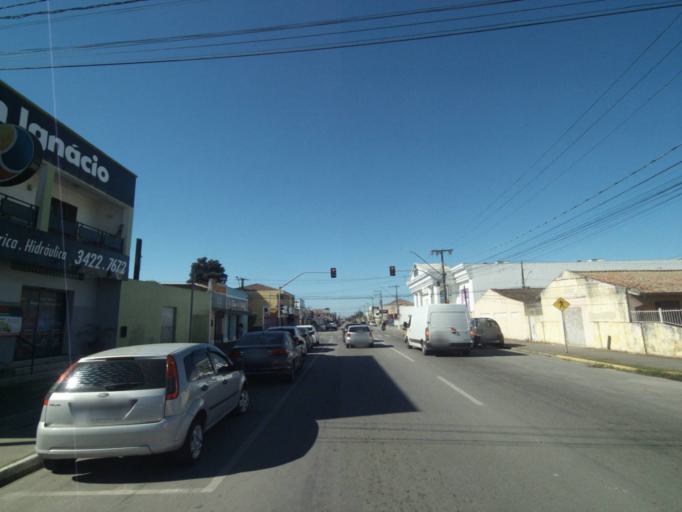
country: BR
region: Parana
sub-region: Paranagua
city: Paranagua
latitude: -25.5275
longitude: -48.5236
